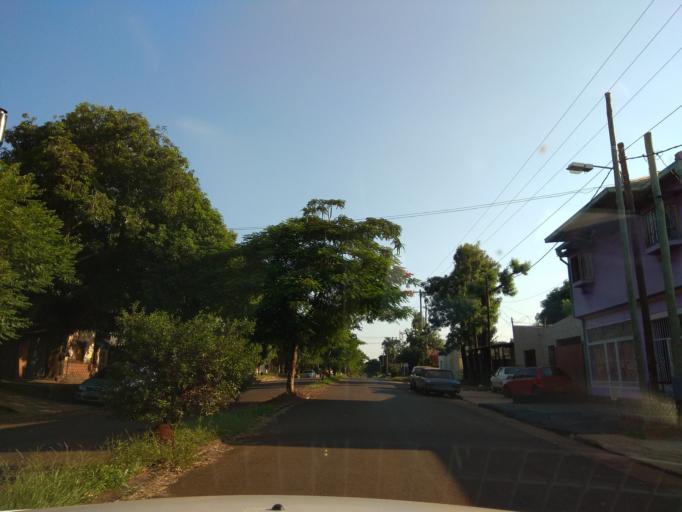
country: AR
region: Misiones
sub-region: Departamento de Capital
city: Posadas
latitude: -27.3689
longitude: -55.9282
